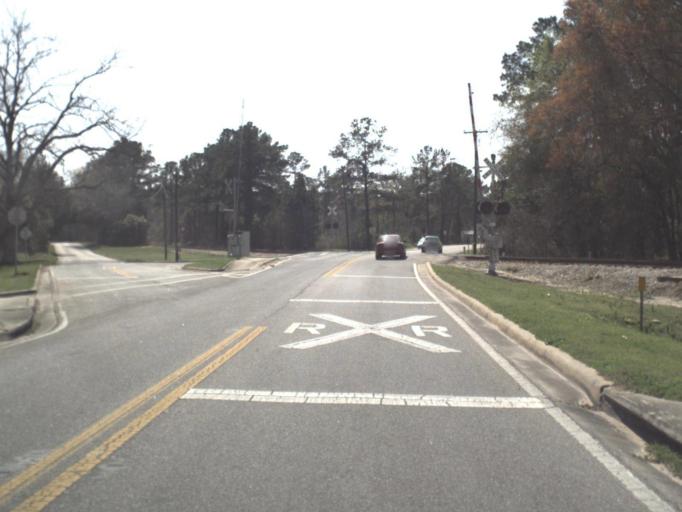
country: US
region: Florida
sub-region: Gadsden County
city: Havana
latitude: 30.6237
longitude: -84.4176
